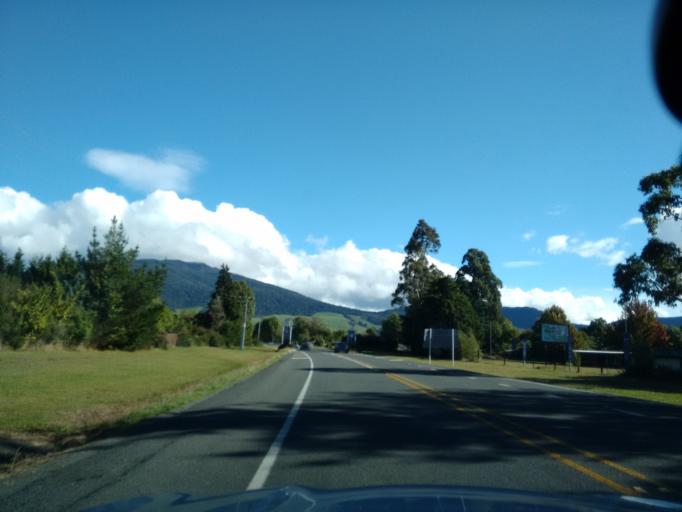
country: NZ
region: Waikato
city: Turangi
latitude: -38.9920
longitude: 175.8087
